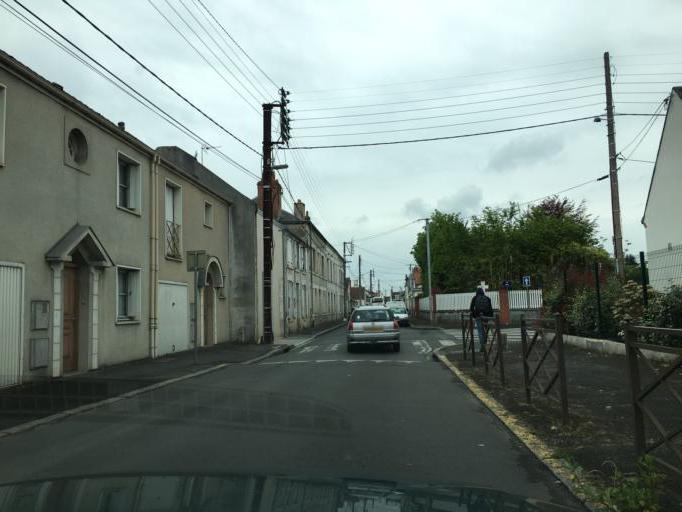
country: FR
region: Centre
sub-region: Departement du Loiret
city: Orleans
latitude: 47.9255
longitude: 1.8895
